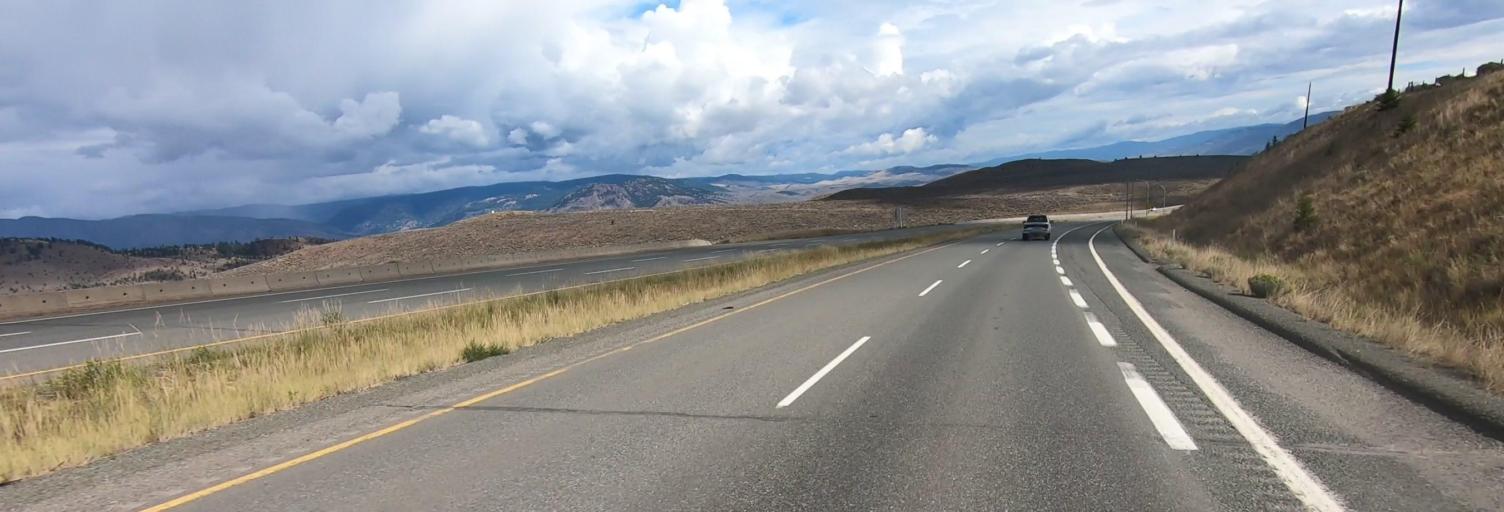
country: CA
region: British Columbia
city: Kamloops
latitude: 50.6536
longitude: -120.4845
